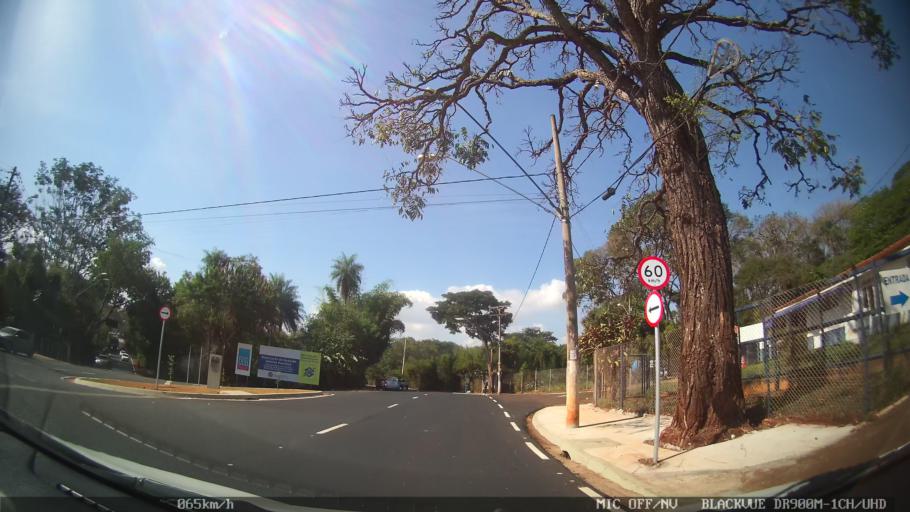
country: BR
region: Sao Paulo
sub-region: Ribeirao Preto
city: Ribeirao Preto
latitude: -21.2059
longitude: -47.8290
